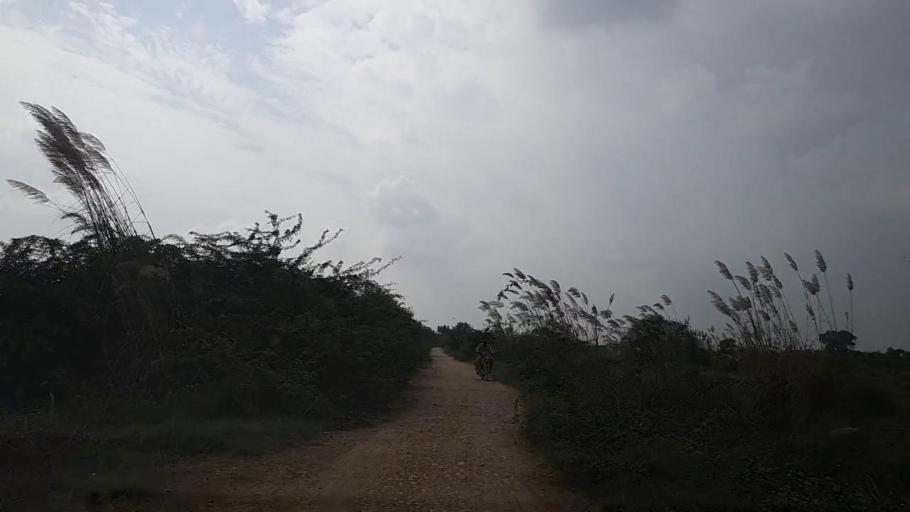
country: PK
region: Sindh
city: Mirpur Batoro
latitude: 24.5978
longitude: 68.1321
